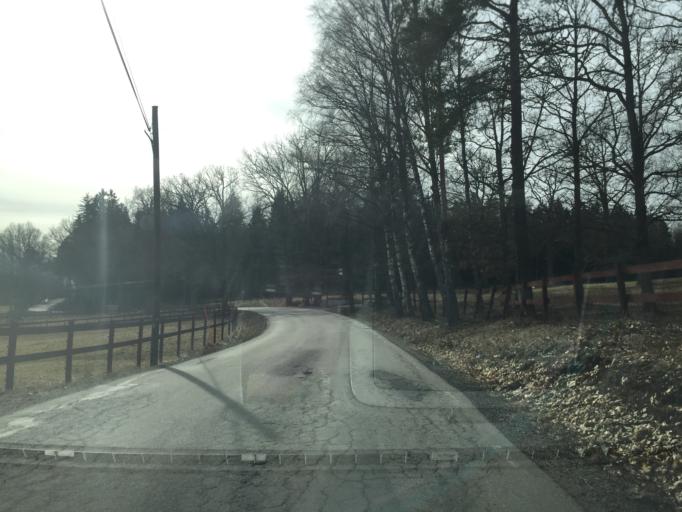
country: SE
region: Stockholm
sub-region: Botkyrka Kommun
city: Tullinge
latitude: 59.1079
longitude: 17.9757
